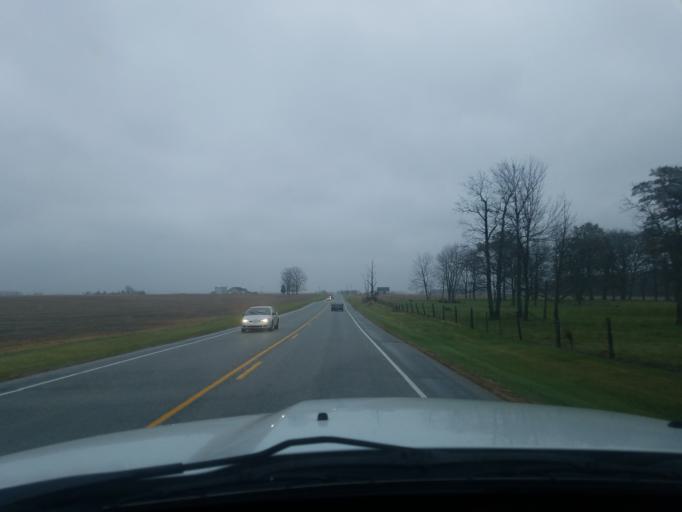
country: US
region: Indiana
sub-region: Madison County
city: Elwood
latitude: 40.4215
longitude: -85.8175
